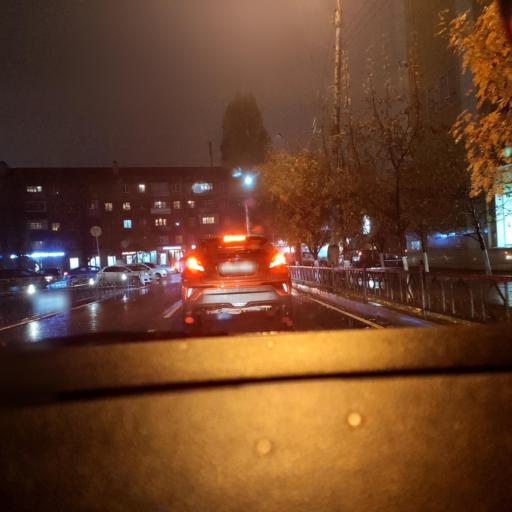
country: RU
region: Voronezj
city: Voronezh
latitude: 51.6600
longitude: 39.1850
